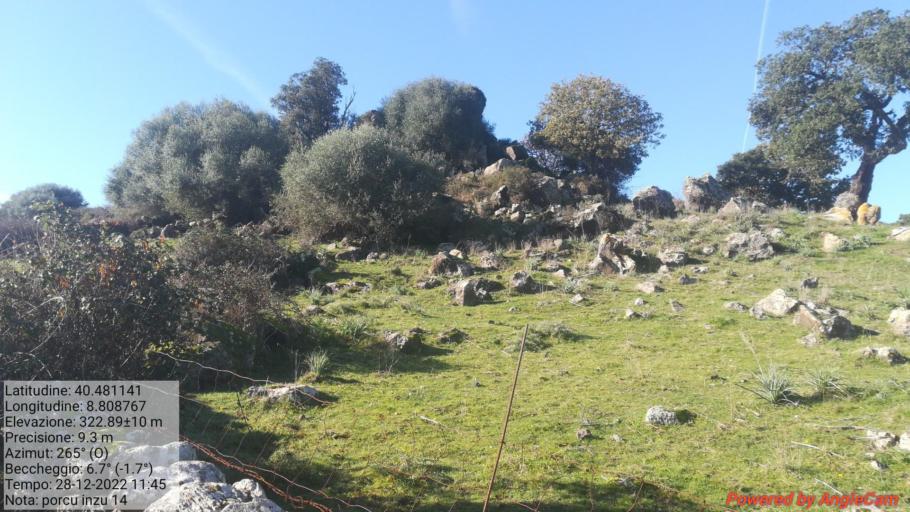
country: IT
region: Sardinia
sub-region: Provincia di Sassari
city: Torralba
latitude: 40.4811
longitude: 8.8088
